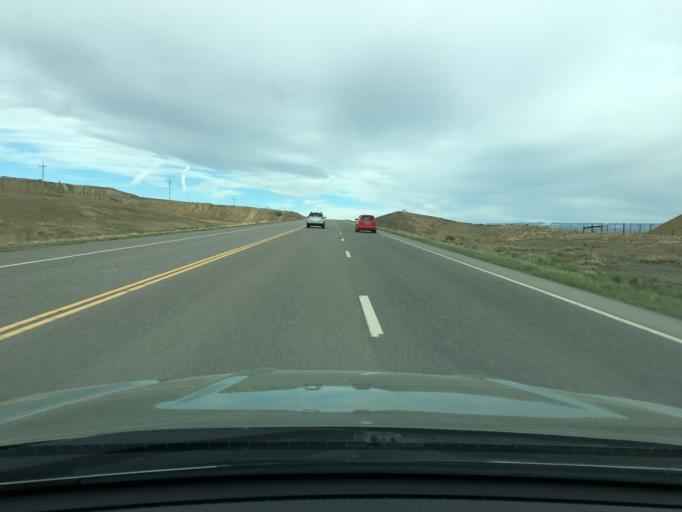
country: US
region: Colorado
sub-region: Delta County
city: Orchard City
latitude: 38.7980
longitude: -107.8448
